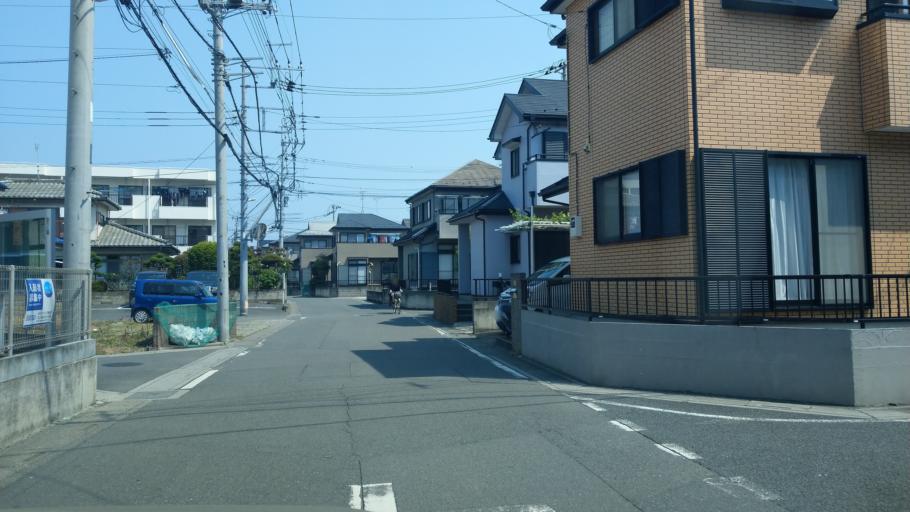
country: JP
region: Saitama
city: Yono
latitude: 35.9095
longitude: 139.5849
